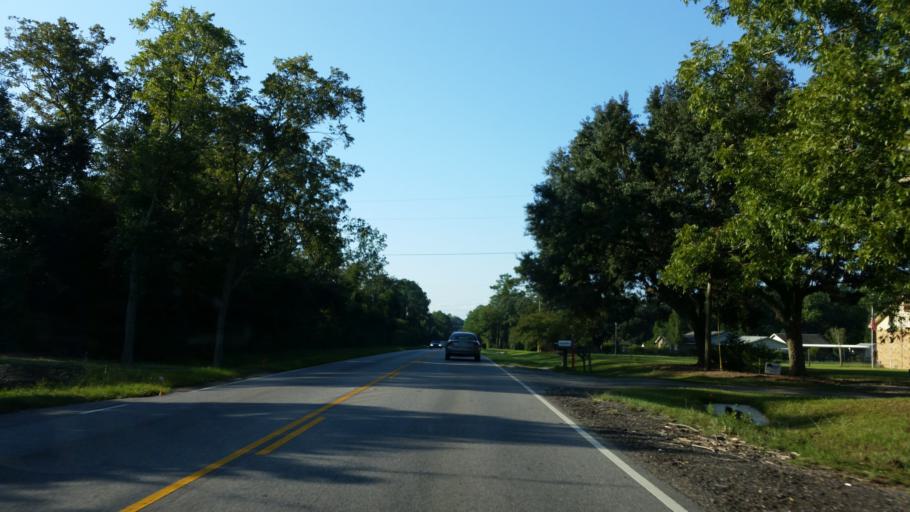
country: US
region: Florida
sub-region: Escambia County
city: Cantonment
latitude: 30.5431
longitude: -87.3804
